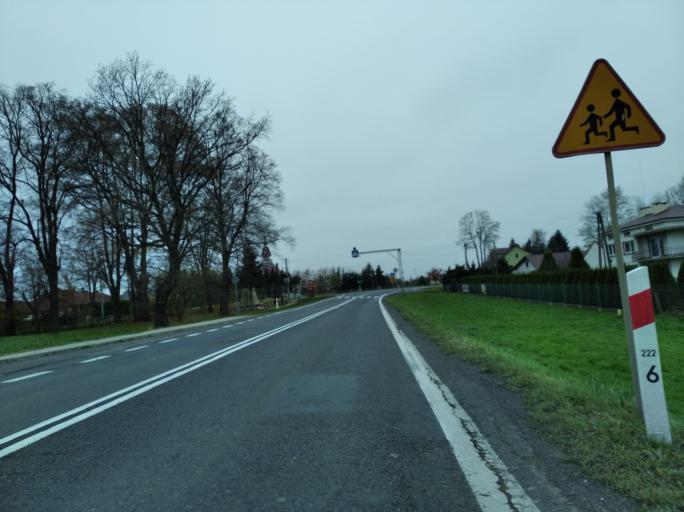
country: PL
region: Subcarpathian Voivodeship
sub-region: Powiat krosnienski
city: Jedlicze
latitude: 49.7396
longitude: 21.6560
